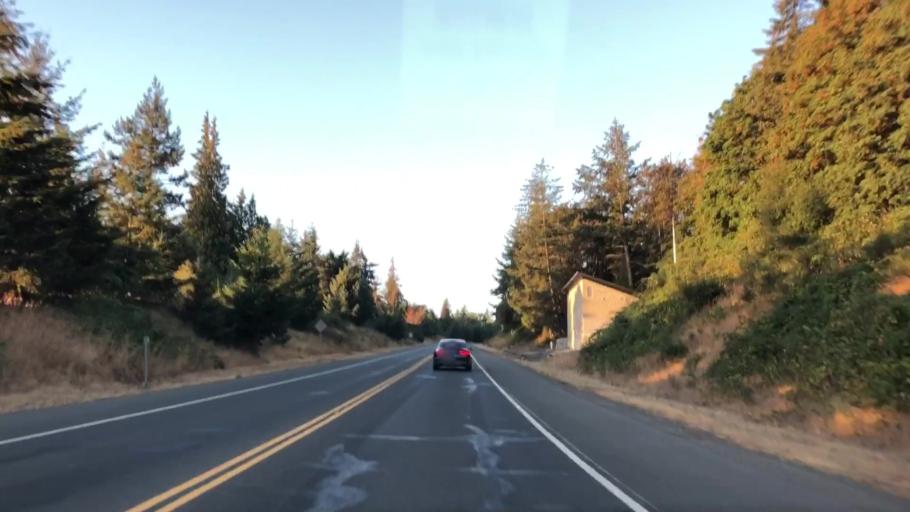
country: CA
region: British Columbia
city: Colwood
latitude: 48.4256
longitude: -123.5021
